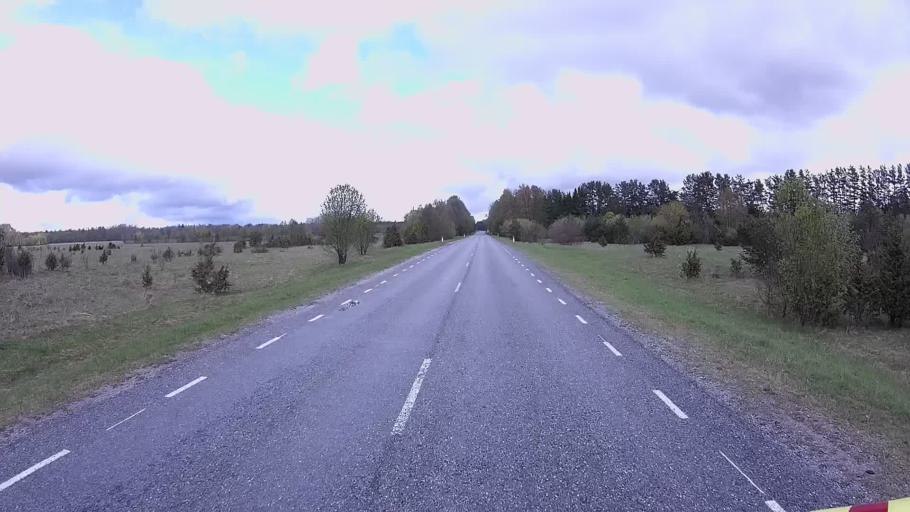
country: EE
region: Hiiumaa
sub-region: Kaerdla linn
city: Kardla
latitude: 58.8060
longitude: 22.7262
